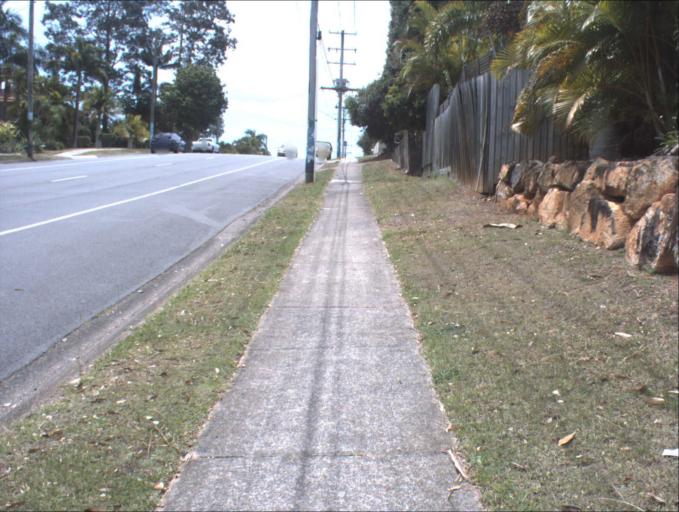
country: AU
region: Queensland
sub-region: Logan
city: Slacks Creek
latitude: -27.6489
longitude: 153.1735
